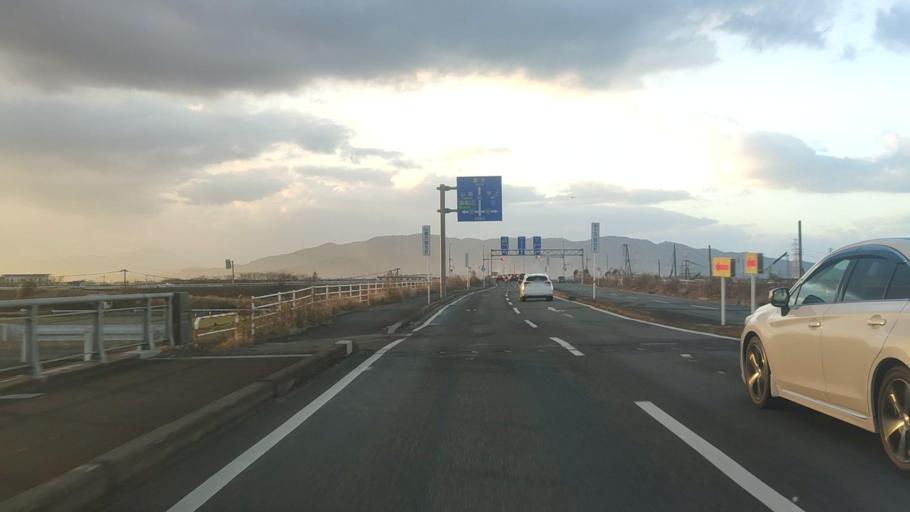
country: JP
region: Kumamoto
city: Kumamoto
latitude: 32.7397
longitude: 130.7047
